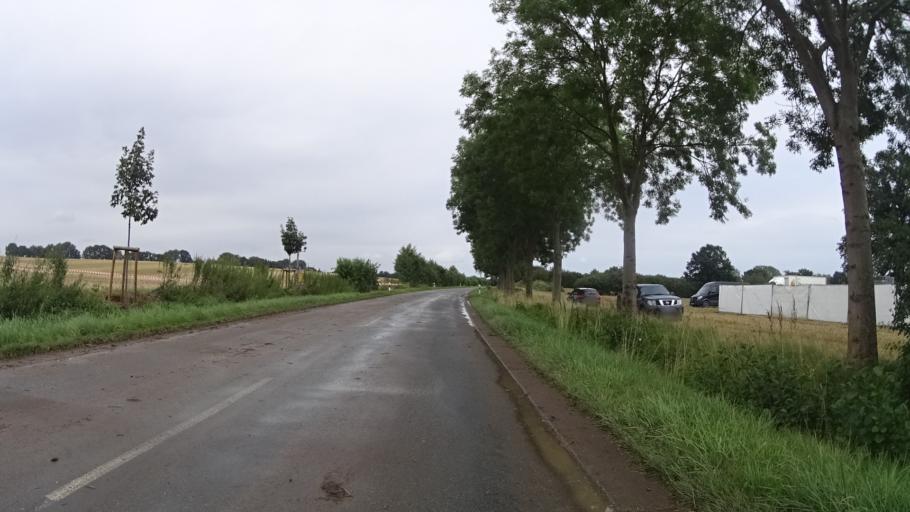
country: DE
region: Schleswig-Holstein
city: Steinhorst
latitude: 53.7161
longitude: 10.4676
